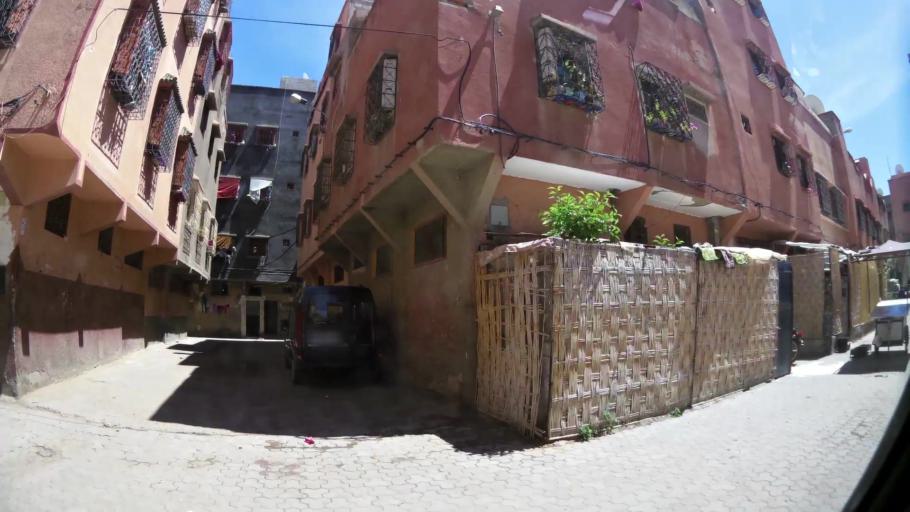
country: MA
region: Marrakech-Tensift-Al Haouz
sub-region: Marrakech
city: Marrakesh
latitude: 31.6548
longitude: -7.9946
